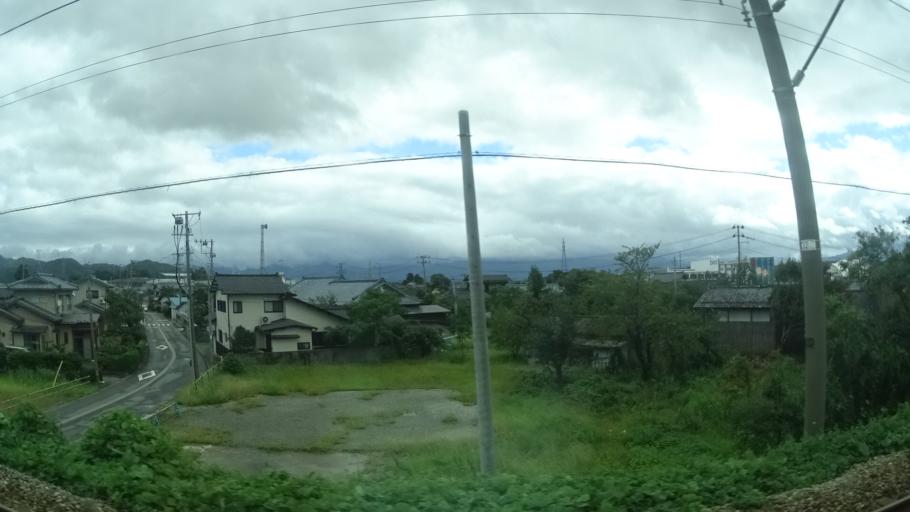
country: JP
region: Niigata
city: Shibata
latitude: 37.9598
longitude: 139.3481
